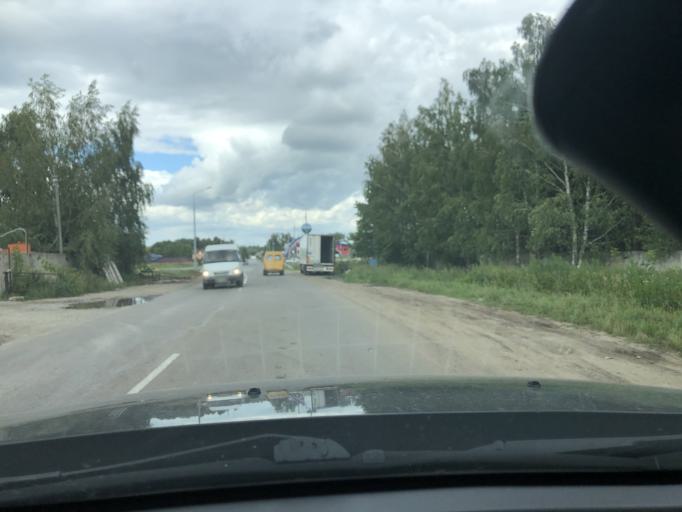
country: RU
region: Tula
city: Kamenetskiy
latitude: 54.0177
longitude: 38.2530
